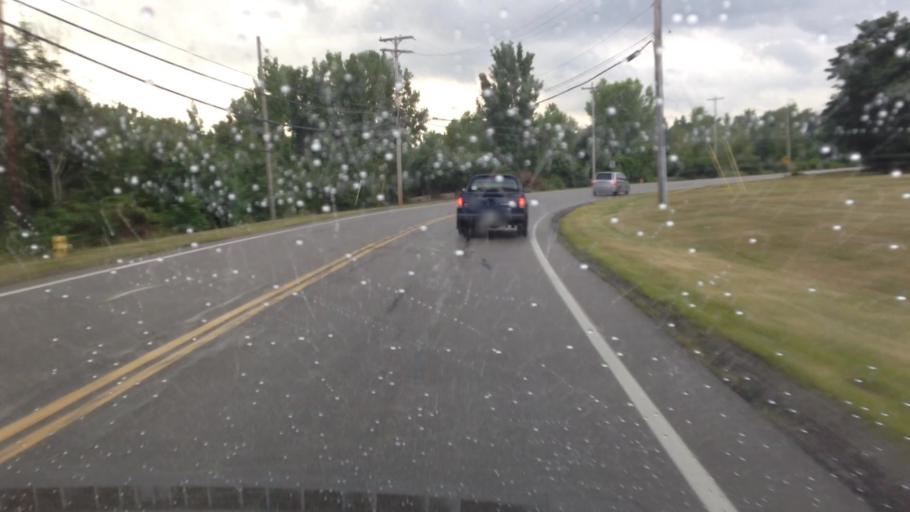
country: US
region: Ohio
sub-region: Summit County
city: Portage Lakes
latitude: 41.0175
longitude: -81.5326
